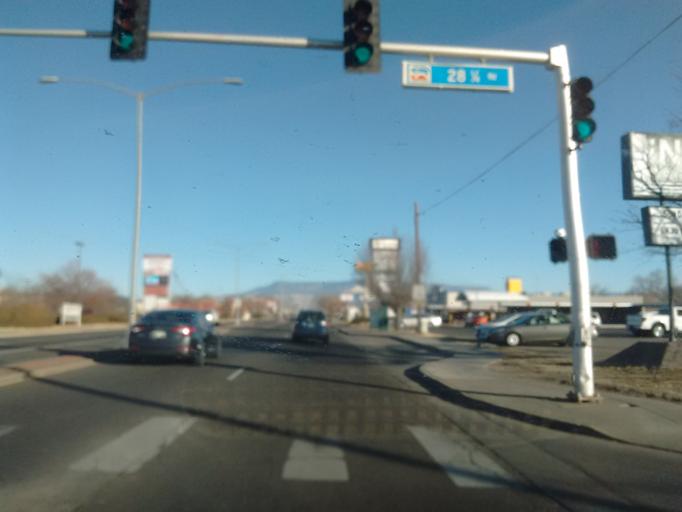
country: US
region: Colorado
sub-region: Mesa County
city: Grand Junction
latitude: 39.0773
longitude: -108.5289
